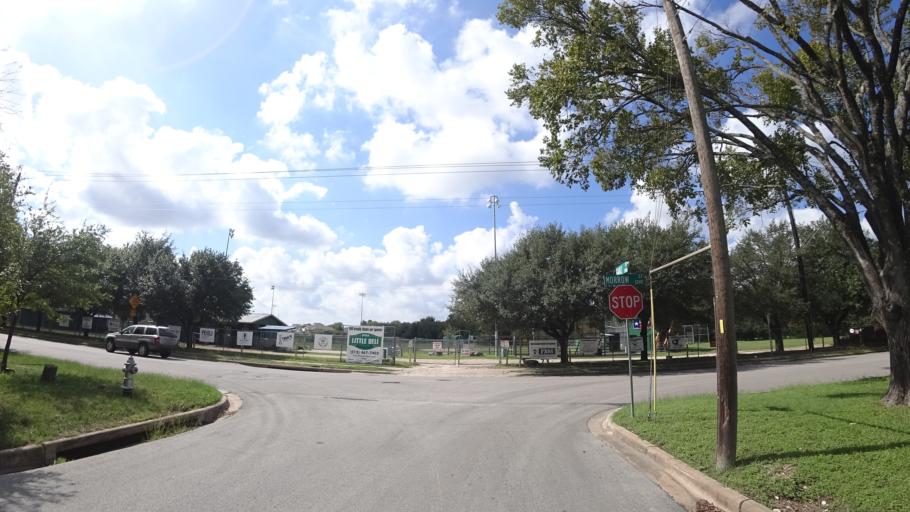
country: US
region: Texas
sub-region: Travis County
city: Austin
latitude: 30.3469
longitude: -97.7207
